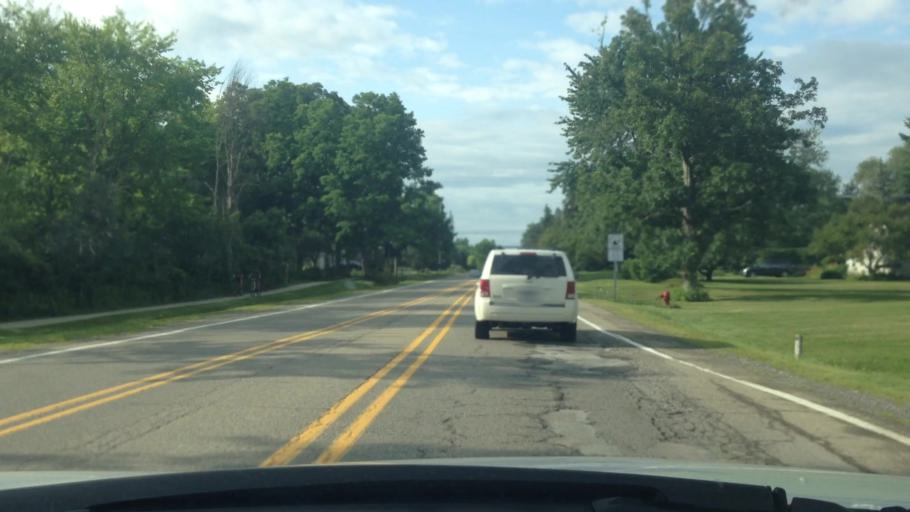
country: US
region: Michigan
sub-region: Oakland County
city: Waterford
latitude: 42.7191
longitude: -83.3493
